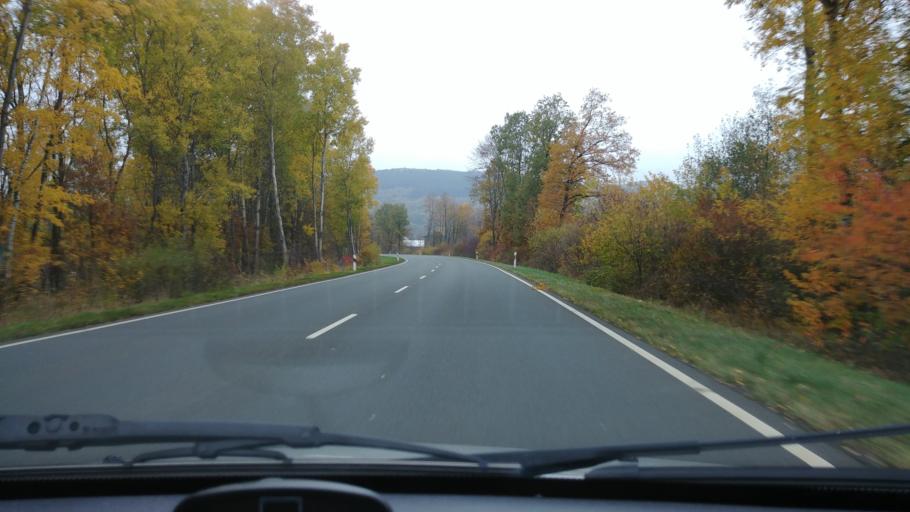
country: DE
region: Rheinland-Pfalz
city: Unnau
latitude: 50.6473
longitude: 7.8915
